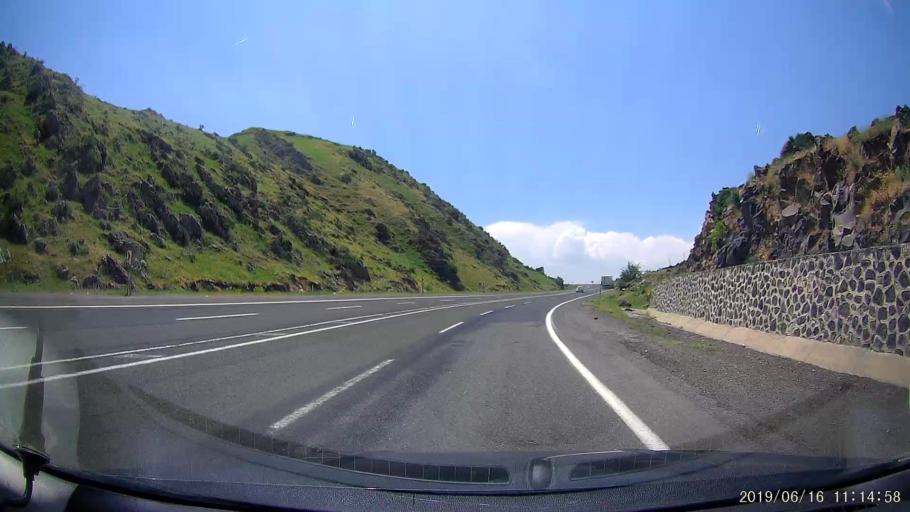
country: TR
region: Igdir
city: Igdir
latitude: 39.7709
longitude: 44.1435
